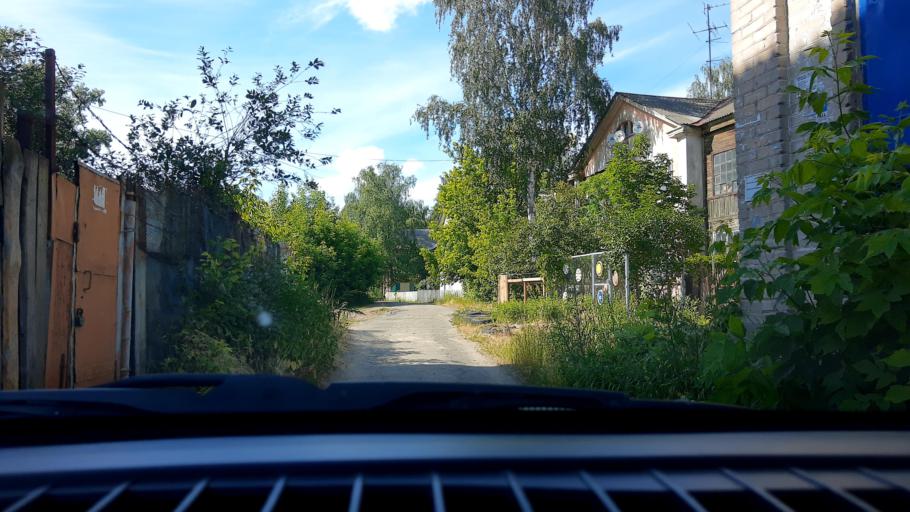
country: RU
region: Nizjnij Novgorod
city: Gorbatovka
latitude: 56.3570
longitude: 43.8440
